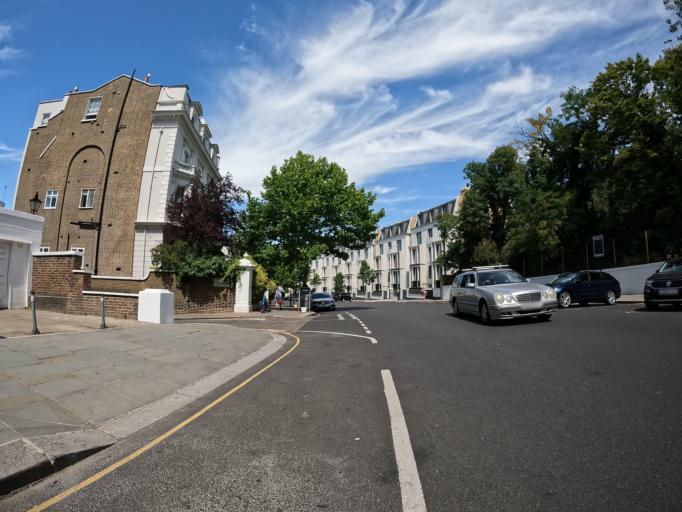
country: GB
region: England
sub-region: Greater London
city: Kensington
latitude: 51.5061
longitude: -0.2040
